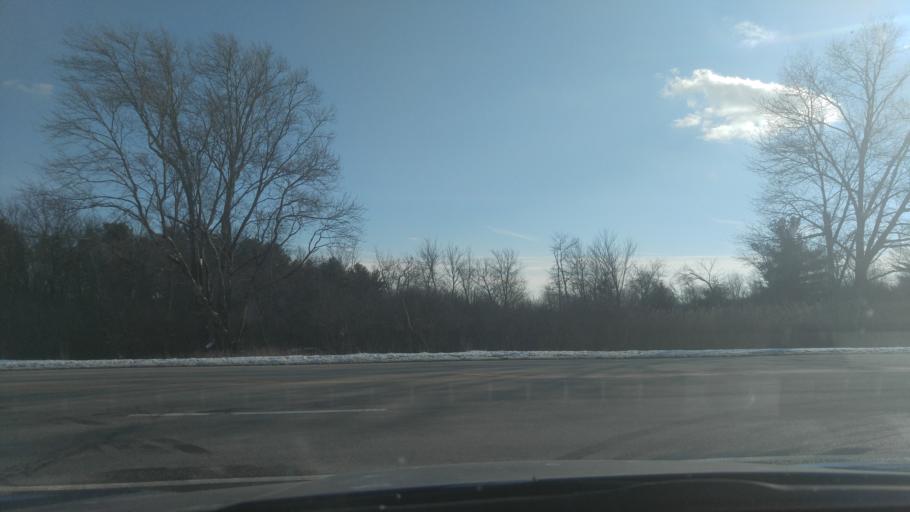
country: US
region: Rhode Island
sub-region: Kent County
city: West Warwick
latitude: 41.6792
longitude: -71.5820
